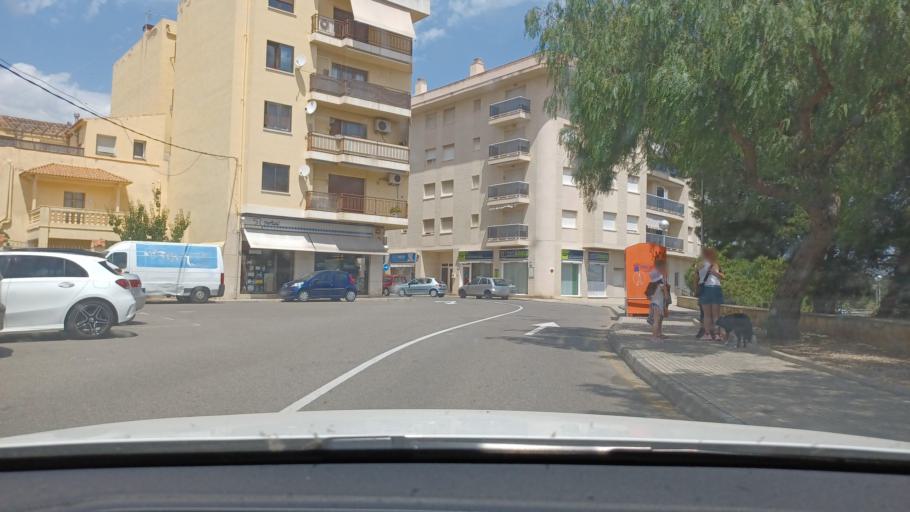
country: ES
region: Catalonia
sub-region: Provincia de Tarragona
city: Colldejou
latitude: 40.9922
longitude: 0.9240
